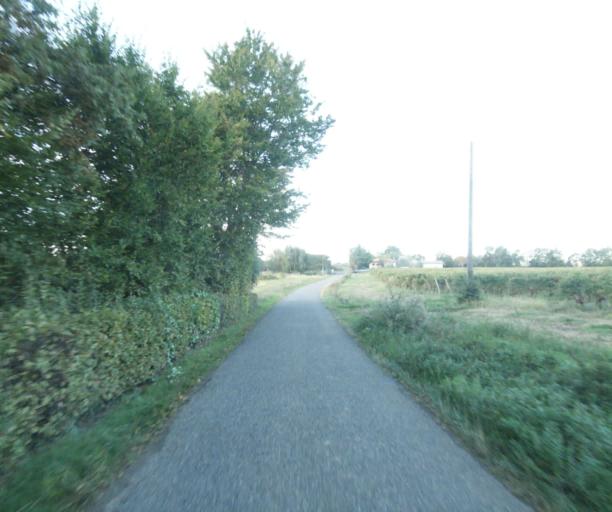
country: FR
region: Midi-Pyrenees
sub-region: Departement du Gers
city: Nogaro
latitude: 43.8317
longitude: -0.0846
